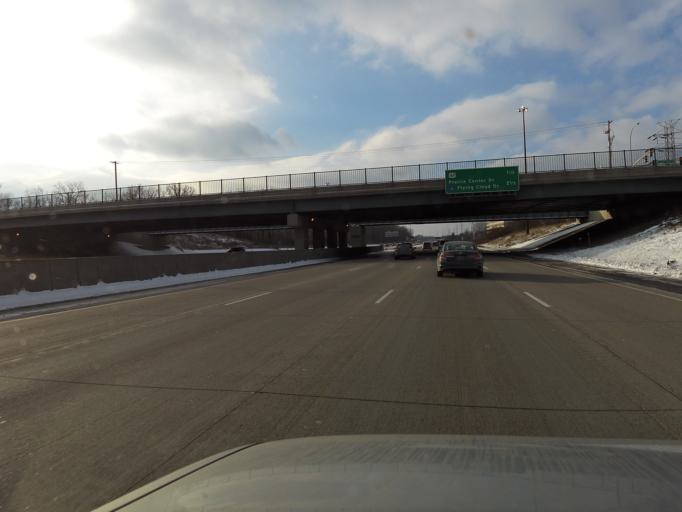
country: US
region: Minnesota
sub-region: Hennepin County
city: Edina
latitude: 44.8597
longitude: -93.3613
